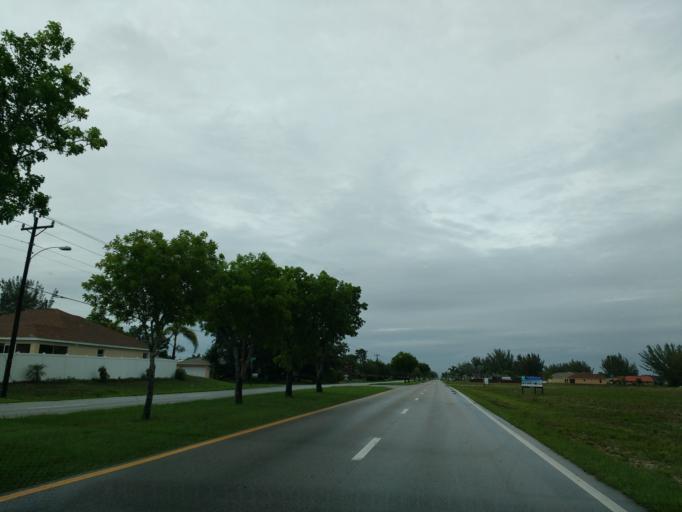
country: US
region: Florida
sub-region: Lee County
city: Cape Coral
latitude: 26.6103
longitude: -82.0070
